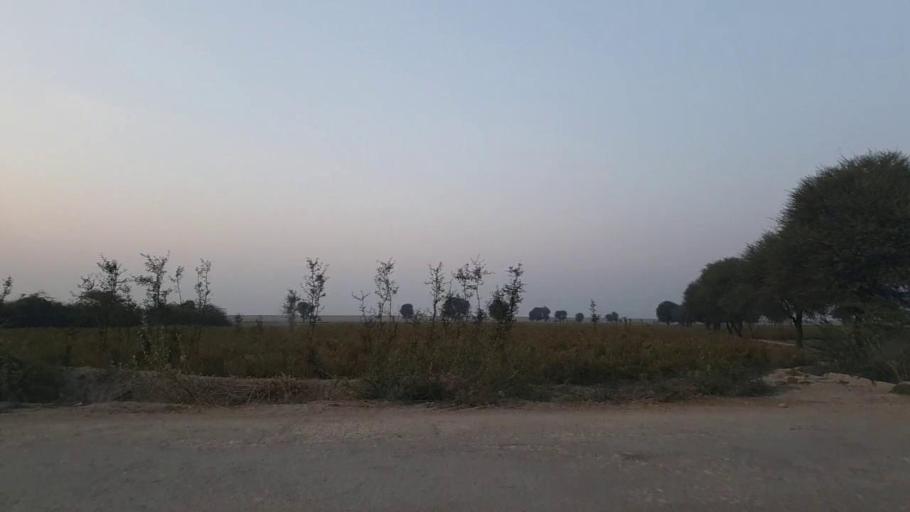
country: PK
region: Sindh
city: Naukot
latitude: 25.0024
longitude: 69.4245
